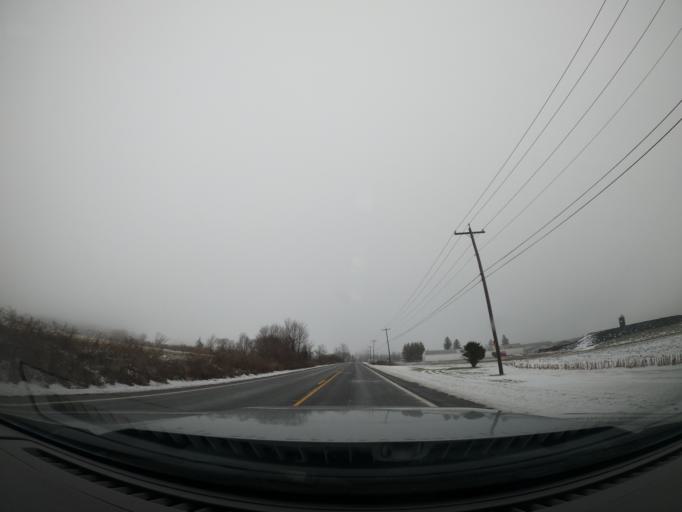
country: US
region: New York
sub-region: Onondaga County
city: Nedrow
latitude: 42.8271
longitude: -76.0435
